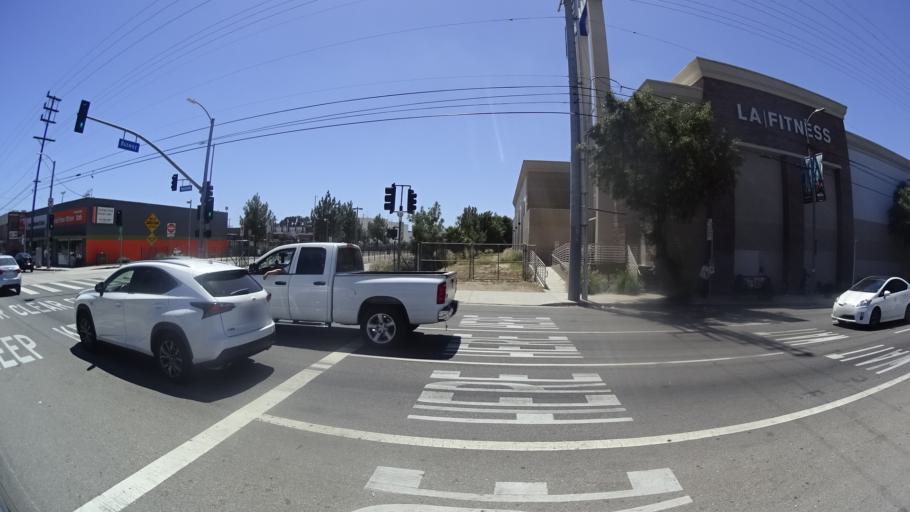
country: US
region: California
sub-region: Los Angeles County
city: Van Nuys
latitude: 34.1806
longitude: -118.4662
